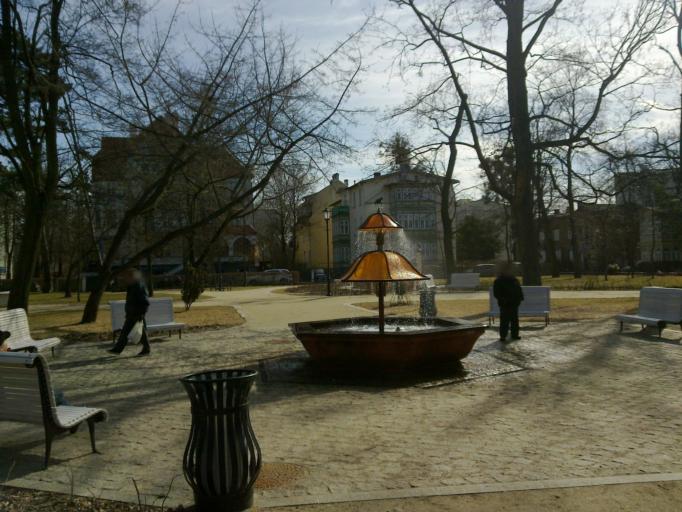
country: PL
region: Pomeranian Voivodeship
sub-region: Sopot
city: Sopot
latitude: 54.4436
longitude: 18.5719
